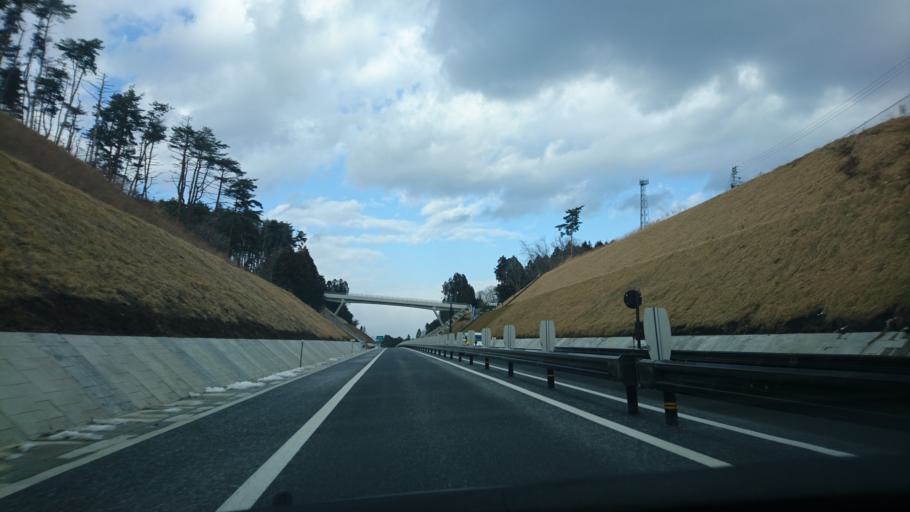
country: JP
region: Miyagi
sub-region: Oshika Gun
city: Onagawa Cho
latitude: 38.7304
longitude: 141.5177
